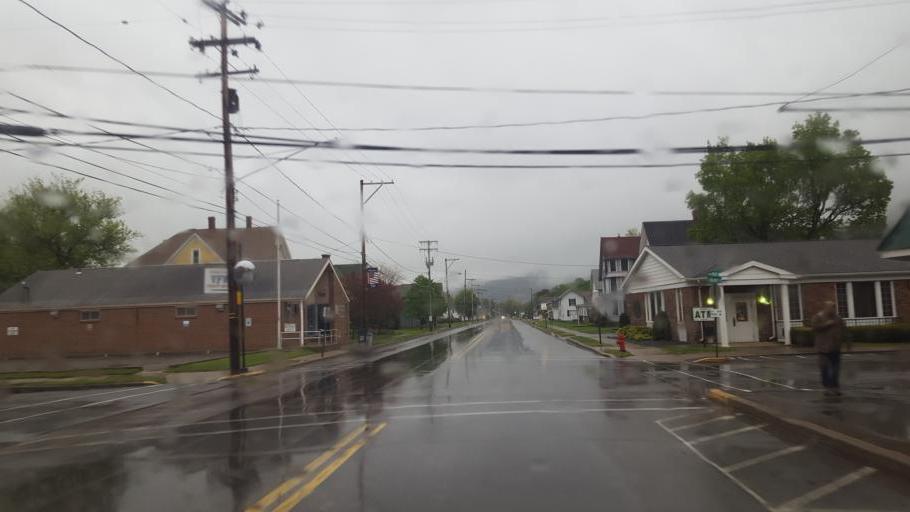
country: US
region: Pennsylvania
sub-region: Tioga County
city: Westfield
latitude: 41.9572
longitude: -77.4400
